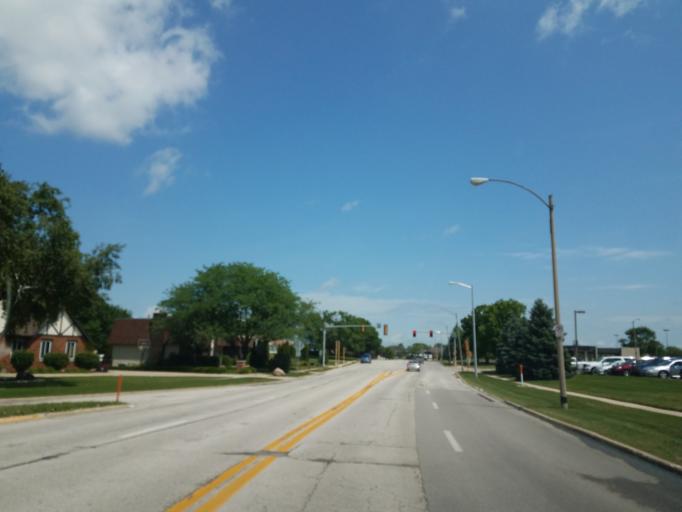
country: US
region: Illinois
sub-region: McLean County
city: Bloomington
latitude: 40.4829
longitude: -88.9607
